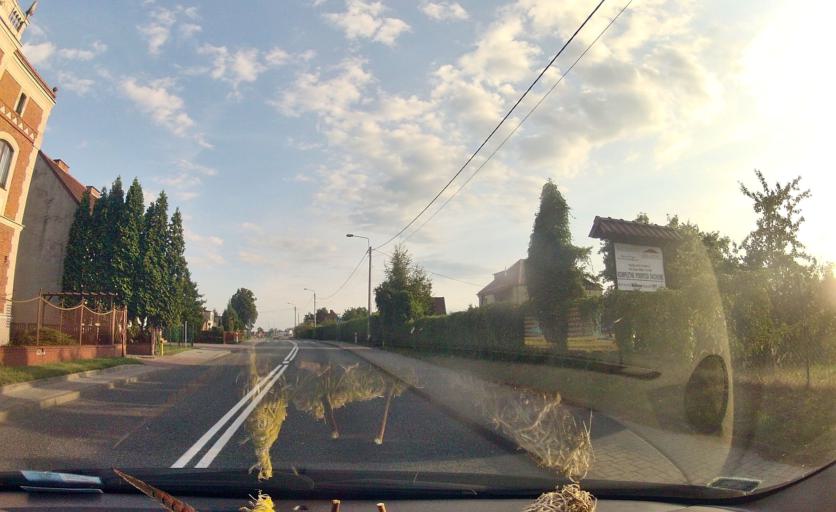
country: PL
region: Opole Voivodeship
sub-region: Powiat kluczborski
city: Kluczbork
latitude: 50.9619
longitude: 18.2189
